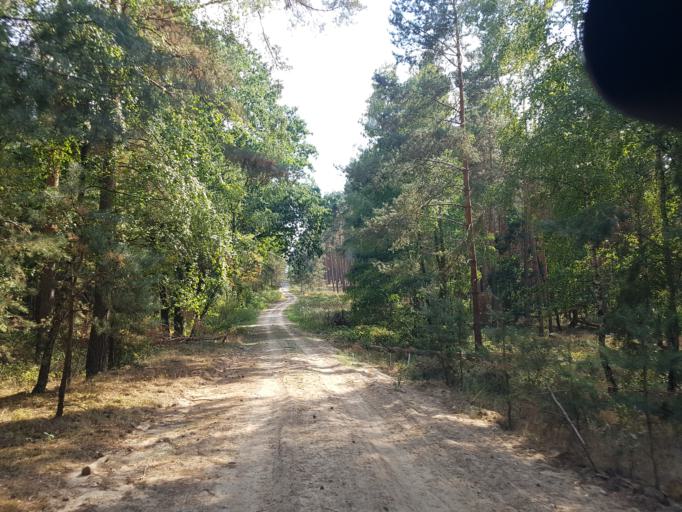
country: DE
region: Brandenburg
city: Treuenbrietzen
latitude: 52.0182
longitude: 12.8630
